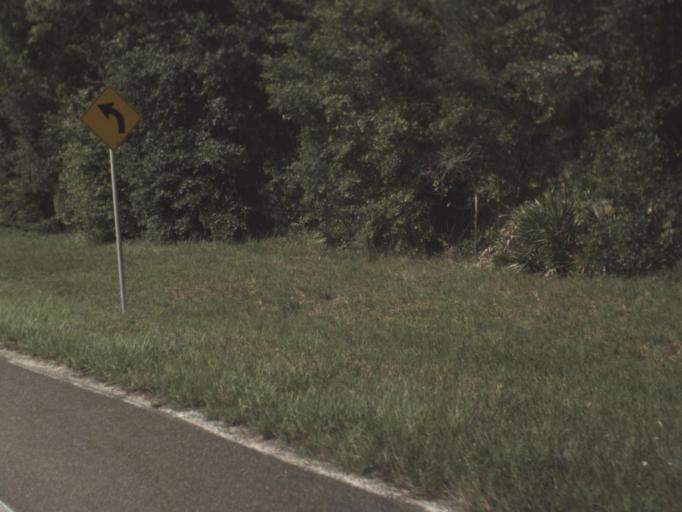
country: US
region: Florida
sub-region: Hardee County
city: Wauchula
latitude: 27.4860
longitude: -82.0146
